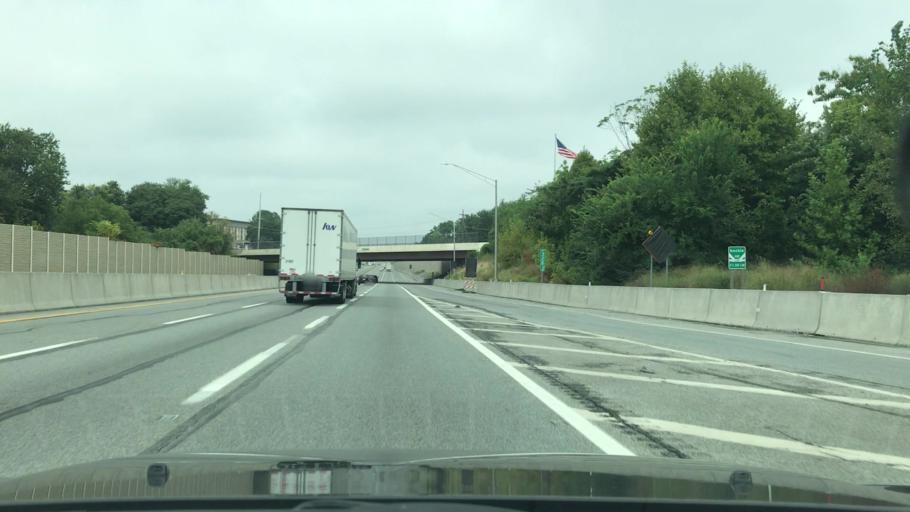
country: US
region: Pennsylvania
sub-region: Montgomery County
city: King of Prussia
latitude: 40.0898
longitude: -75.3741
